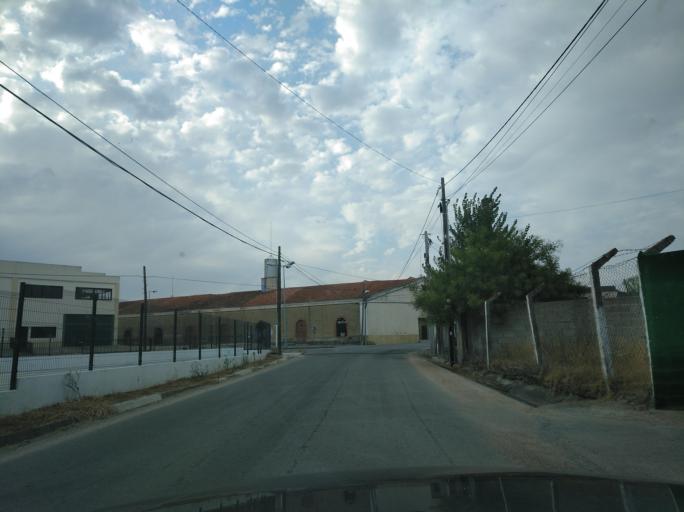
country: PT
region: Portalegre
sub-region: Elvas
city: Elvas
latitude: 38.8936
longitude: -7.1432
